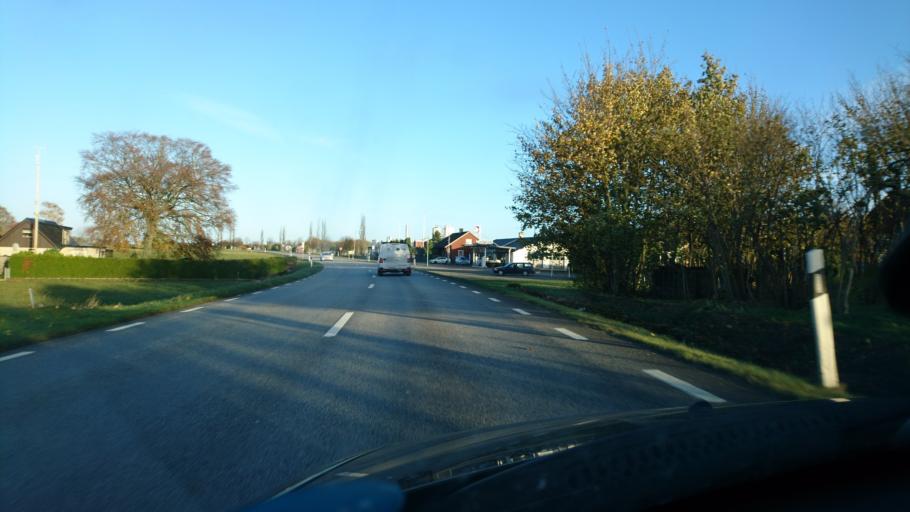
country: SE
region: Skane
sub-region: Tomelilla Kommun
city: Tomelilla
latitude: 55.5433
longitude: 14.0435
